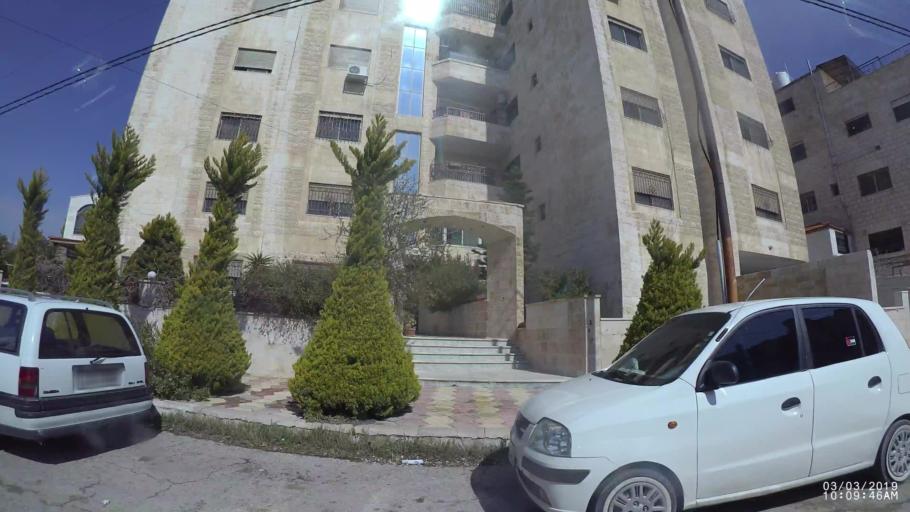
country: JO
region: Amman
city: Al Jubayhah
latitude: 31.9918
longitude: 35.8956
